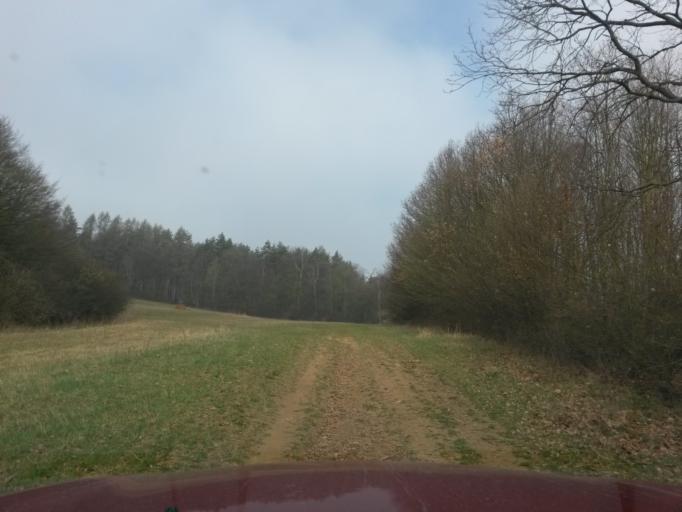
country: SK
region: Presovsky
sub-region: Okres Presov
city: Presov
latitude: 48.9224
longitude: 21.1771
